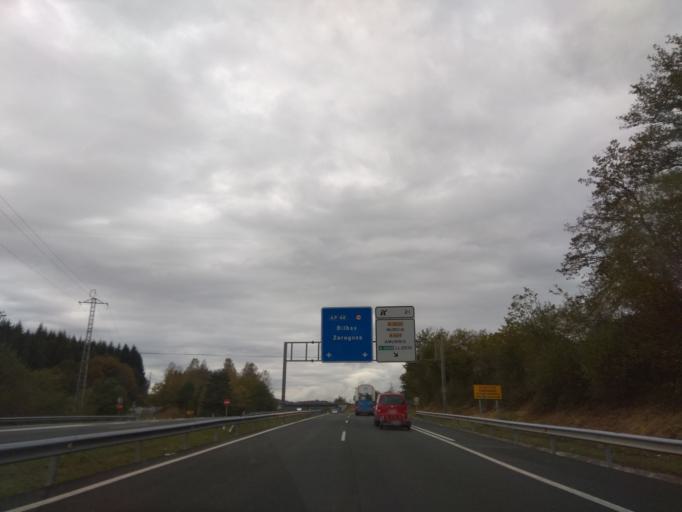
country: ES
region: Basque Country
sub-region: Provincia de Alava
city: Murguia
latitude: 42.9624
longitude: -2.8482
